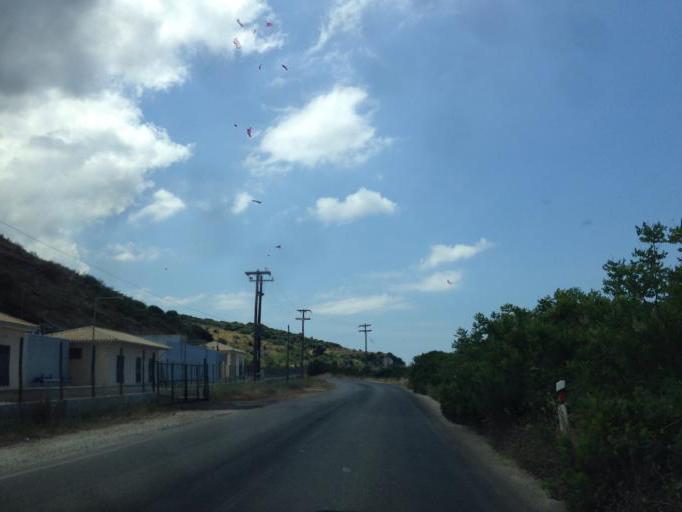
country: GR
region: Ionian Islands
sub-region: Nomos Kerkyras
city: Acharavi
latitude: 39.7919
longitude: 19.9075
